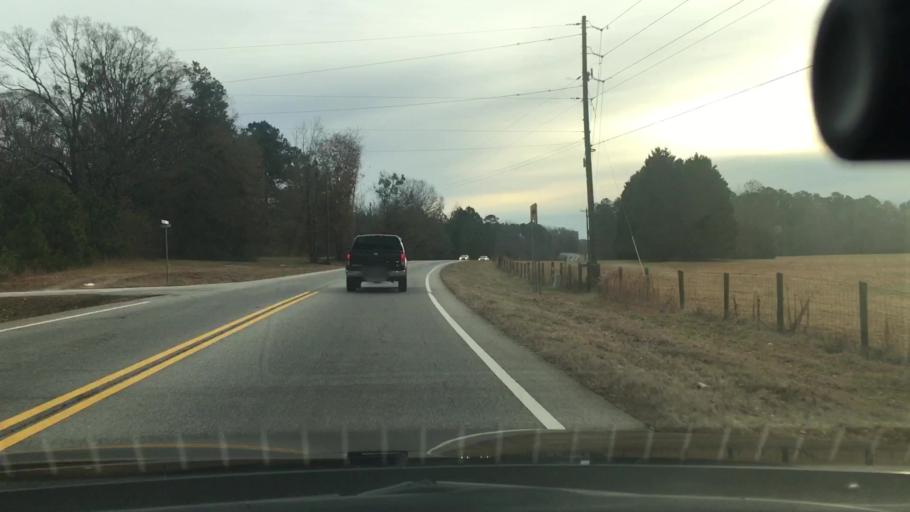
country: US
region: Georgia
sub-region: Spalding County
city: Experiment
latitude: 33.2406
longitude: -84.4128
